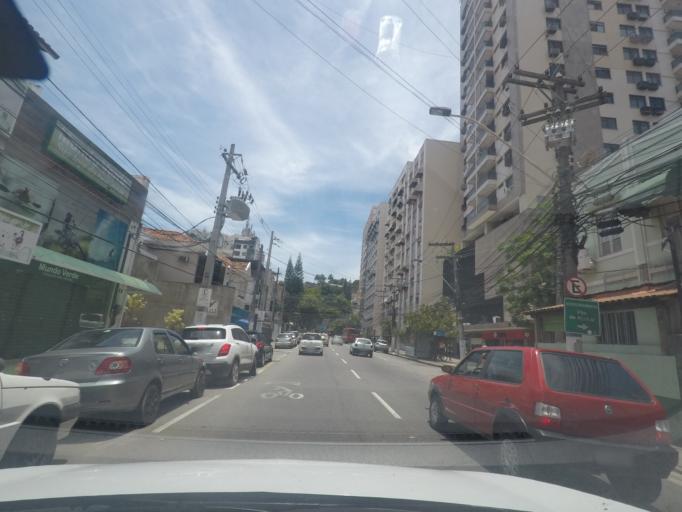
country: BR
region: Rio de Janeiro
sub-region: Niteroi
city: Niteroi
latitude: -22.9031
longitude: -43.1221
